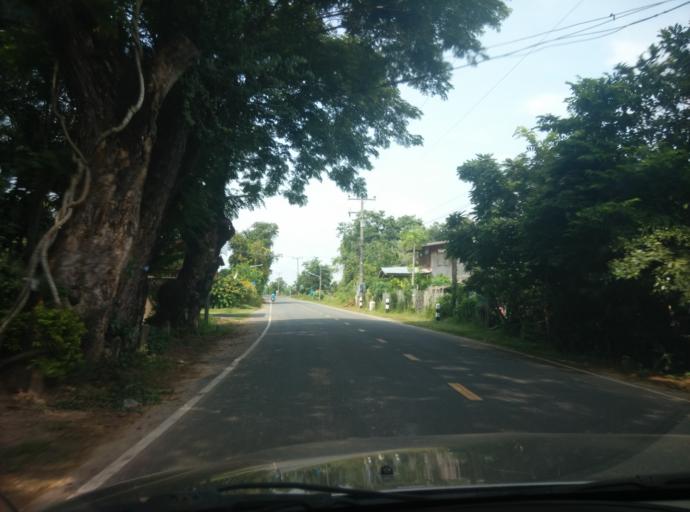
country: TH
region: Sisaket
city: Huai Thap Than
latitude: 14.9894
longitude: 104.0714
